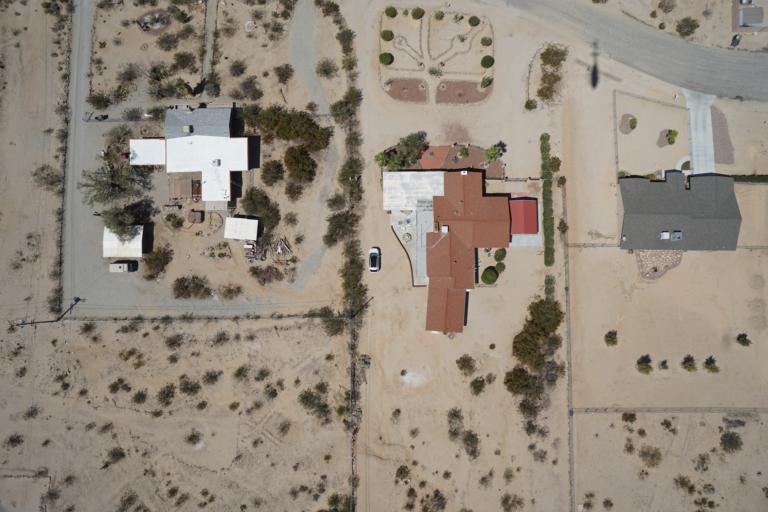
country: US
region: California
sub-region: San Bernardino County
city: Twentynine Palms
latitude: 34.1334
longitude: -116.0341
